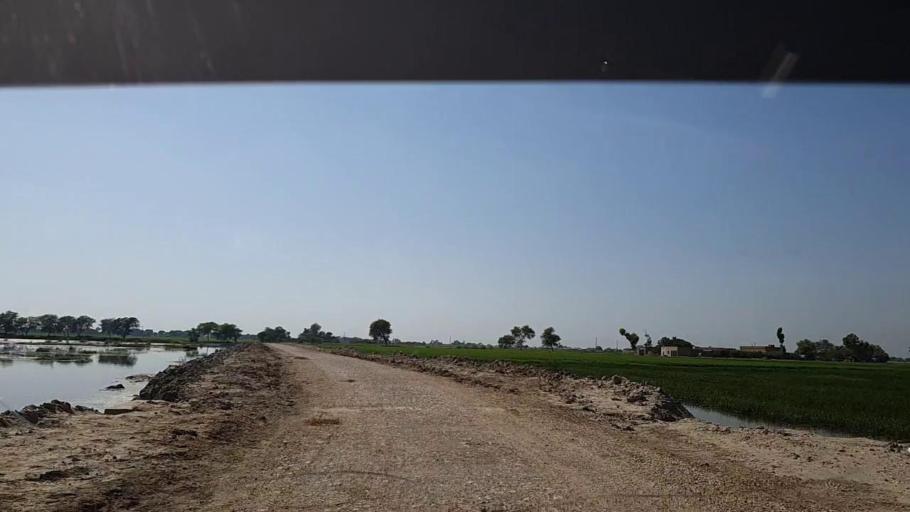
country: PK
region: Sindh
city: Tangwani
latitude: 28.3308
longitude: 69.0749
